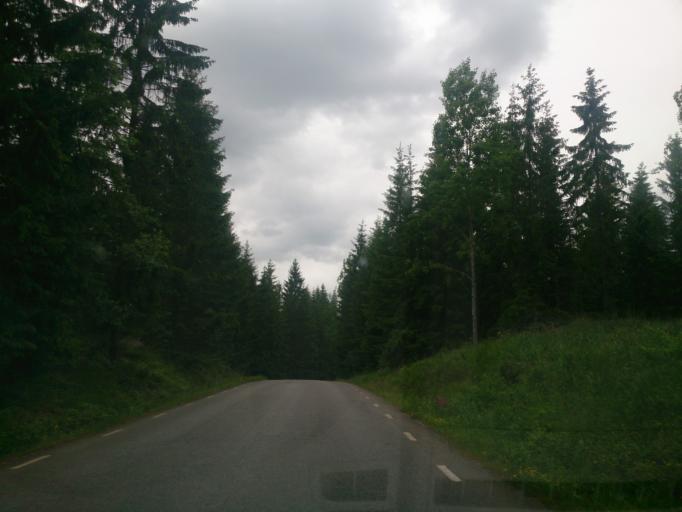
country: SE
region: OEstergoetland
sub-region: Soderkopings Kommun
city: Soederkoeping
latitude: 58.3132
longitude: 16.2882
